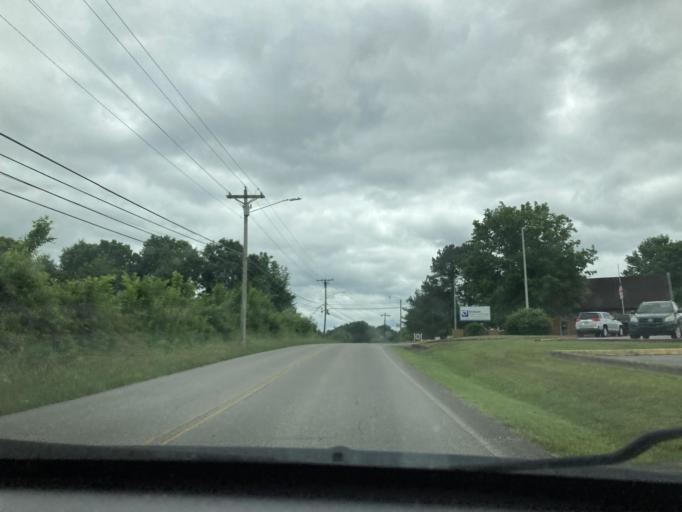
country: US
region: Tennessee
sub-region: Dickson County
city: Dickson
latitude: 36.0877
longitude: -87.3804
